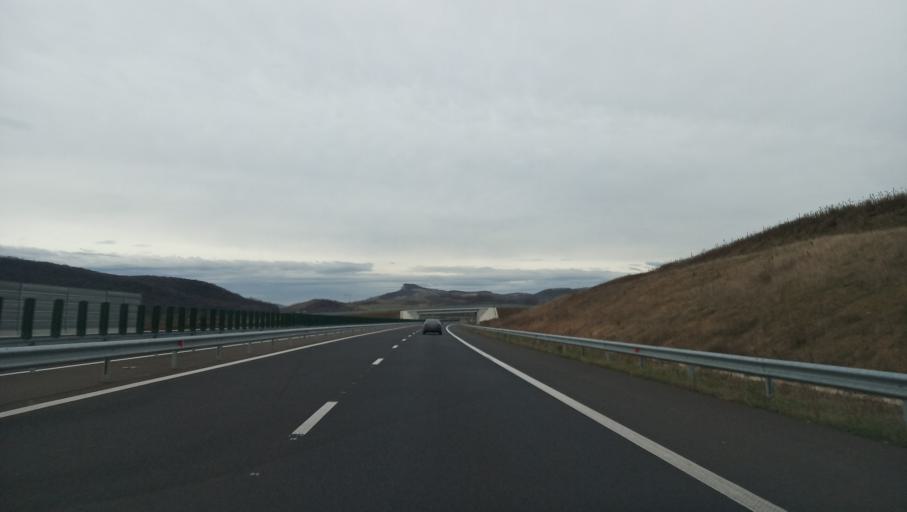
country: RO
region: Hunedoara
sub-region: Comuna Branisca
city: Branisca
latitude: 45.9283
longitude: 22.7677
